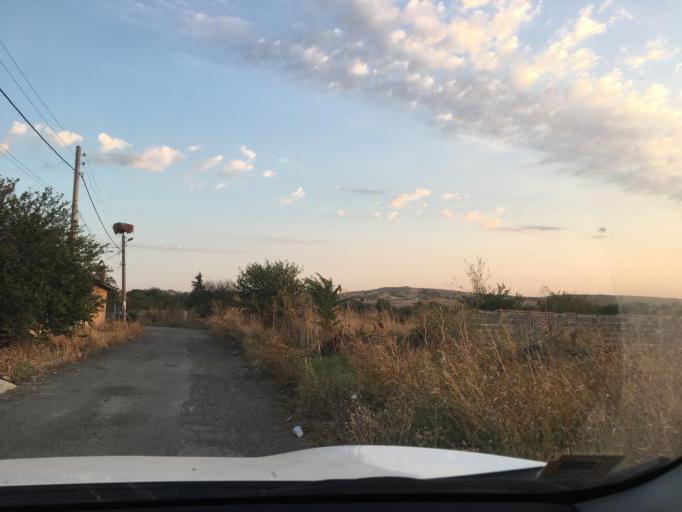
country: BG
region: Burgas
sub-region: Obshtina Burgas
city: Burgas
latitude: 42.6107
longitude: 27.4973
